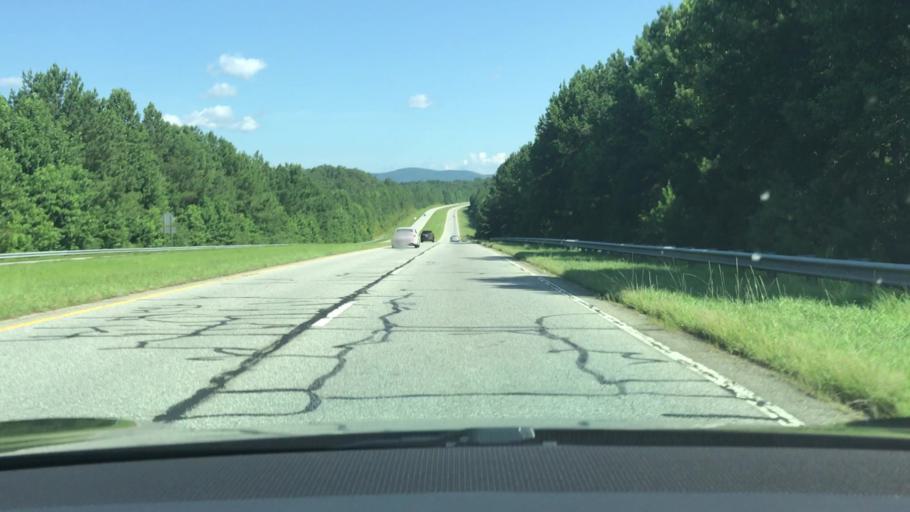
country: US
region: Georgia
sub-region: Habersham County
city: Clarkesville
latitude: 34.6300
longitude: -83.4485
